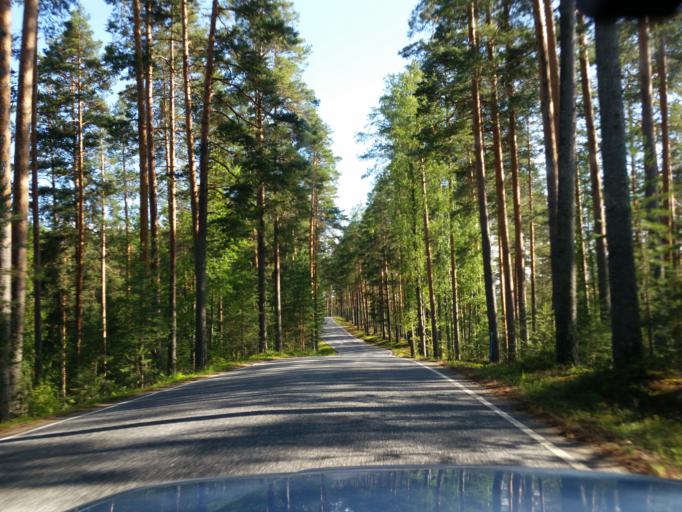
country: FI
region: Southern Savonia
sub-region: Savonlinna
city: Sulkava
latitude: 61.7835
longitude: 28.4254
